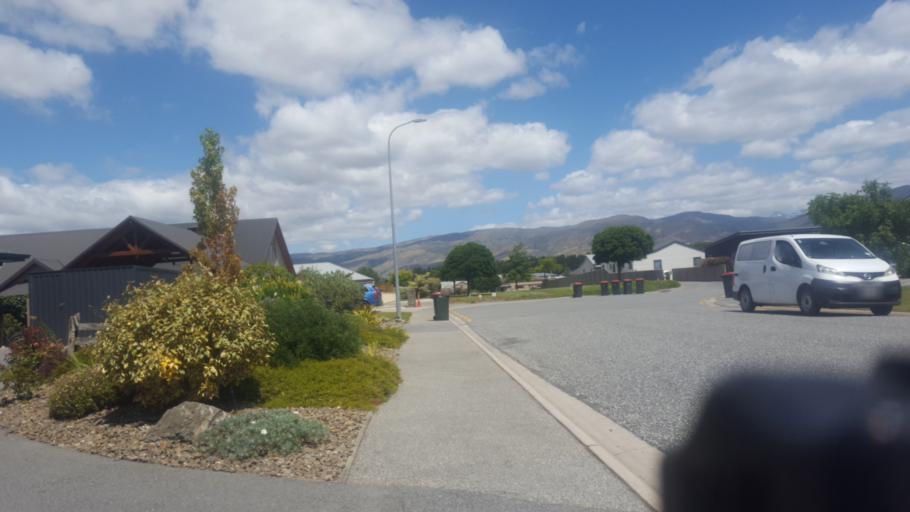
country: NZ
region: Otago
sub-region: Queenstown-Lakes District
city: Wanaka
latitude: -45.0503
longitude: 169.1983
